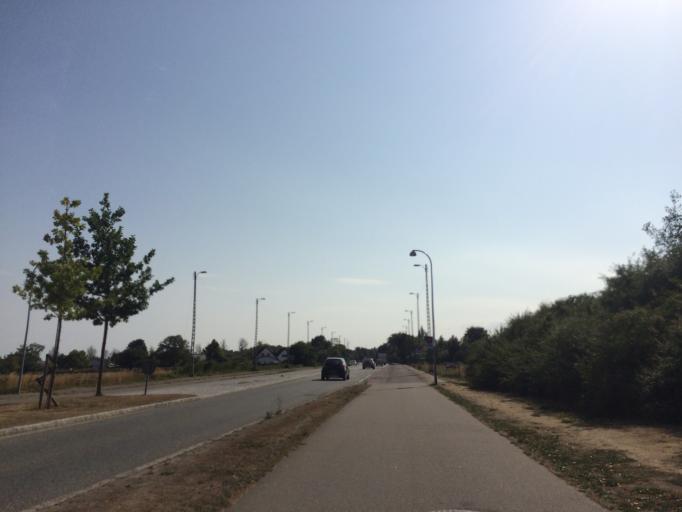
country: DK
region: Capital Region
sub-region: Ishoj Kommune
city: Ishoj
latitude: 55.6043
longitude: 12.3536
